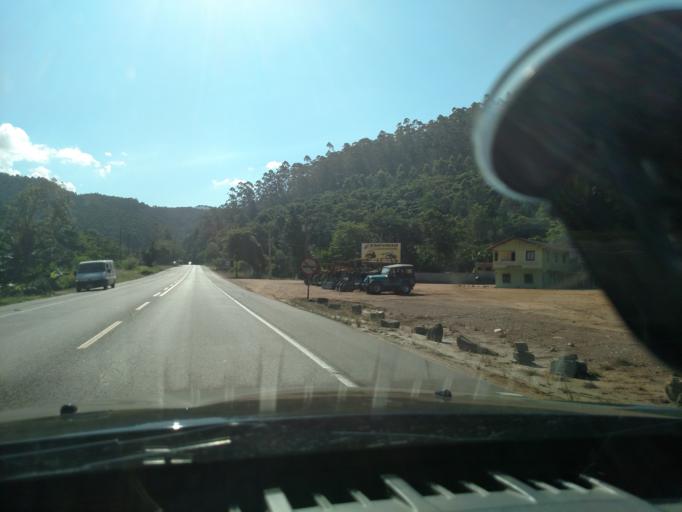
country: BR
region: Santa Catarina
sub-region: Ibirama
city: Ibirama
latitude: -27.0781
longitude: -49.4915
